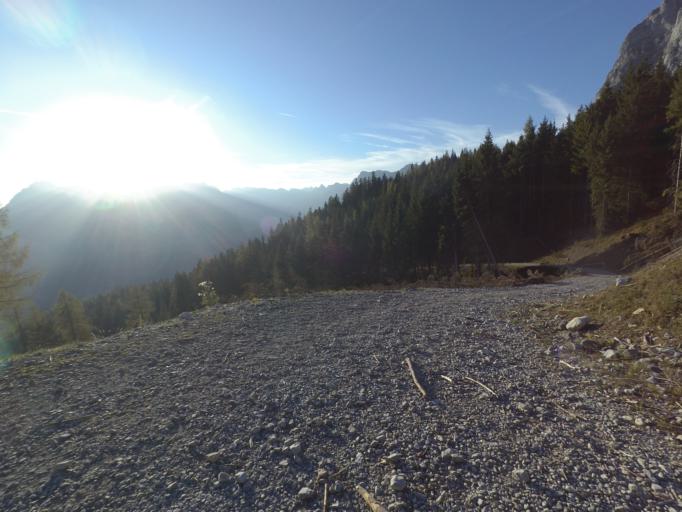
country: AT
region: Salzburg
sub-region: Politischer Bezirk Sankt Johann im Pongau
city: Werfenweng
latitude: 47.4839
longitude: 13.2282
